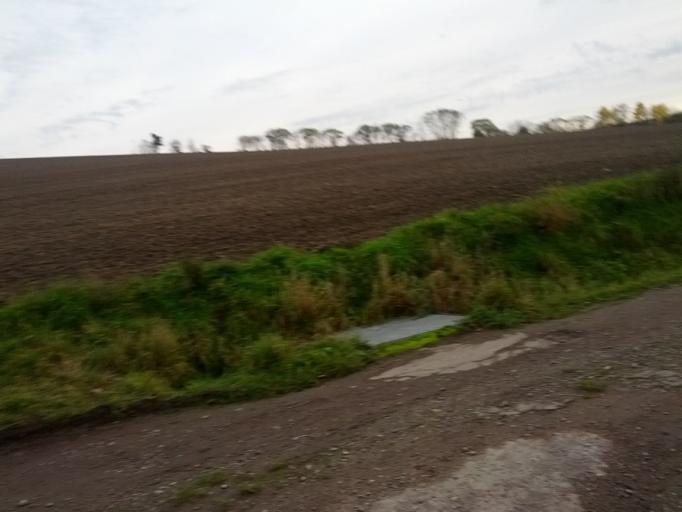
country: DE
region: Thuringia
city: Thal
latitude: 50.9391
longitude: 10.3661
